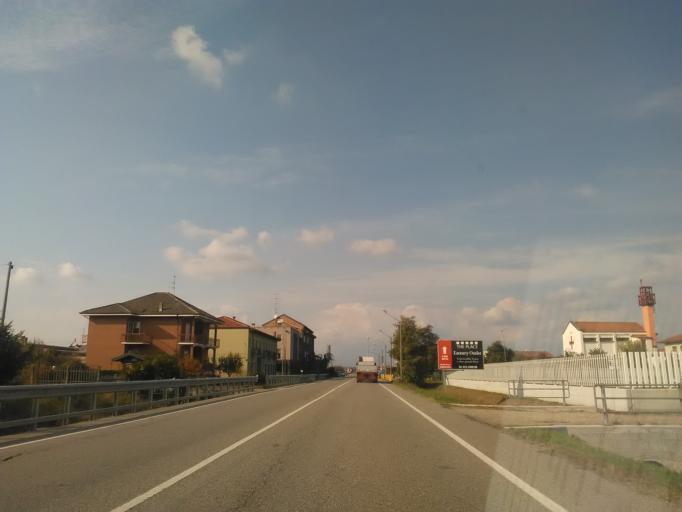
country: IT
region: Piedmont
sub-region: Provincia di Vercelli
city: Balocco
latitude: 45.4439
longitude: 8.2342
